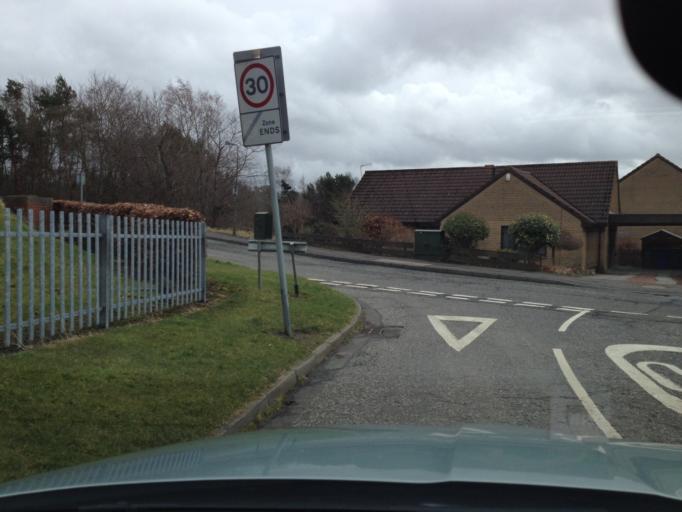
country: GB
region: Scotland
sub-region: West Lothian
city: Livingston
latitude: 55.8933
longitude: -3.5304
